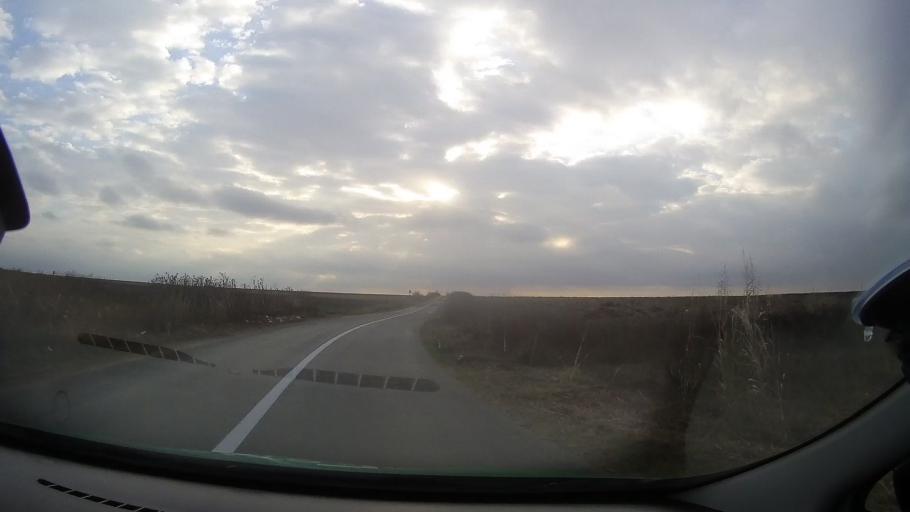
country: RO
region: Constanta
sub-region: Comuna Pestera
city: Pestera
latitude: 44.1330
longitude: 28.1193
